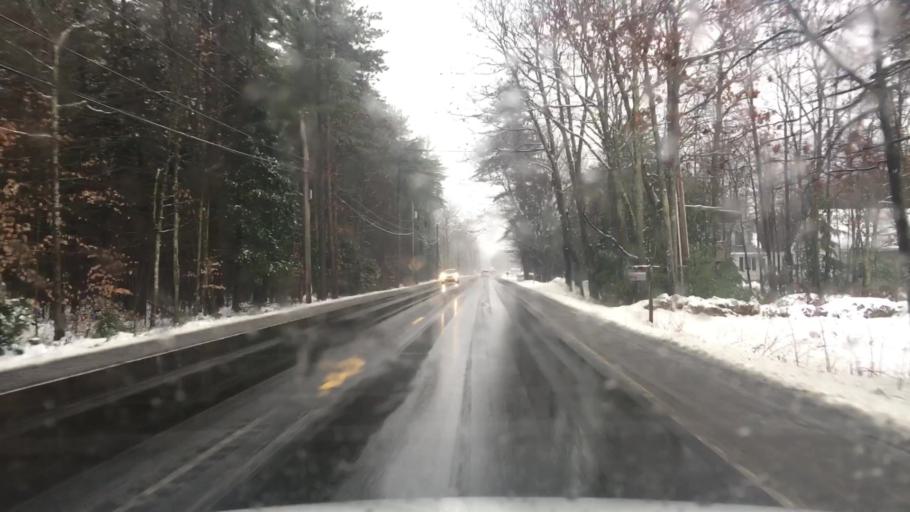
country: US
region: Maine
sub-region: York County
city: Buxton
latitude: 43.7211
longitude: -70.5276
